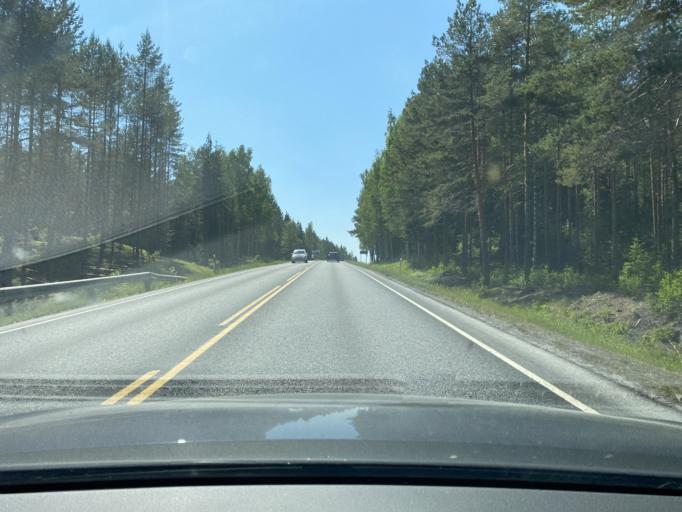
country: FI
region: Pirkanmaa
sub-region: Tampere
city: Nokia
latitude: 61.4105
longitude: 23.3021
